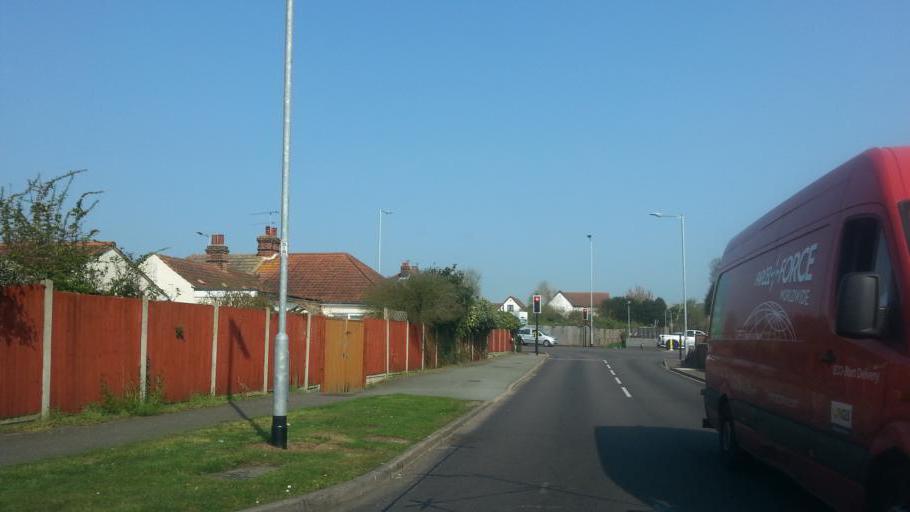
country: GB
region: England
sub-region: Suffolk
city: Kesgrave
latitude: 52.0632
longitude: 1.2170
